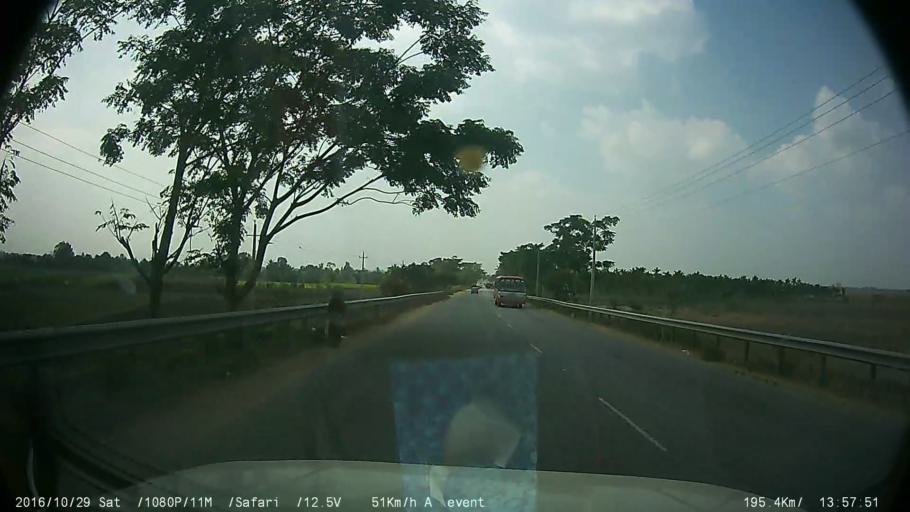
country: IN
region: Karnataka
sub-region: Mysore
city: Piriyapatna
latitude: 12.3350
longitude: 76.1520
